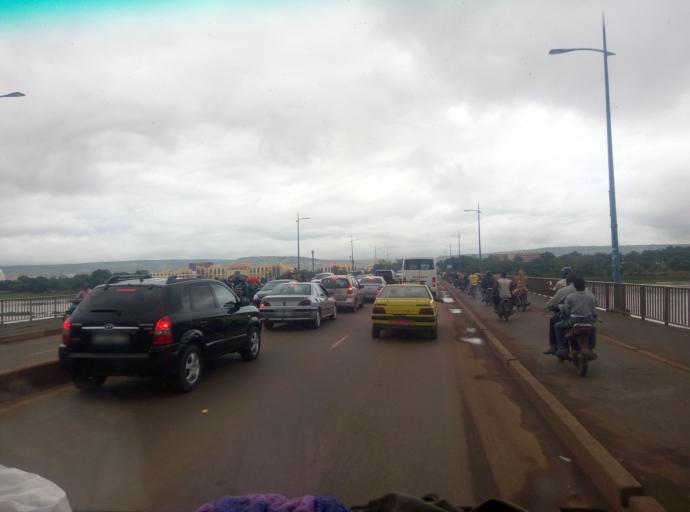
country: ML
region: Bamako
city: Bamako
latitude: 12.6241
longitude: -8.0051
